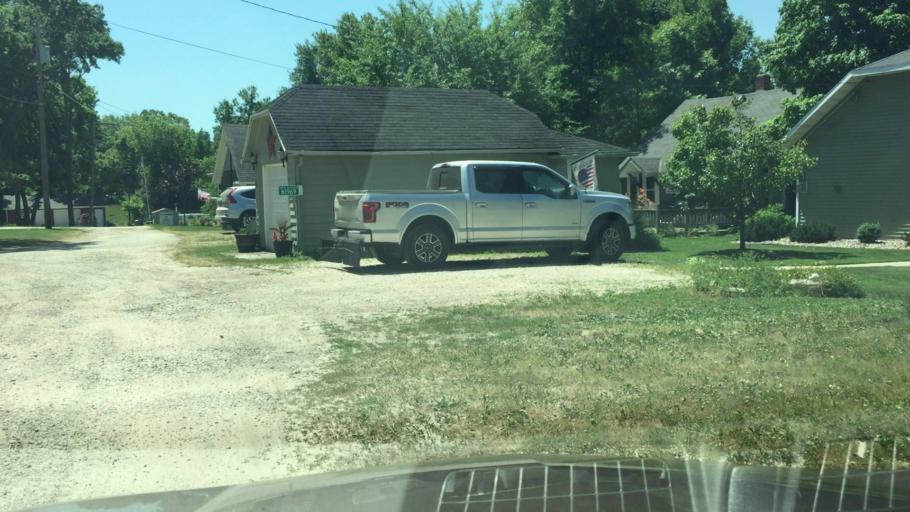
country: US
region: Wisconsin
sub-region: Fond du Lac County
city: Saint Peter
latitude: 43.9606
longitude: -88.3190
